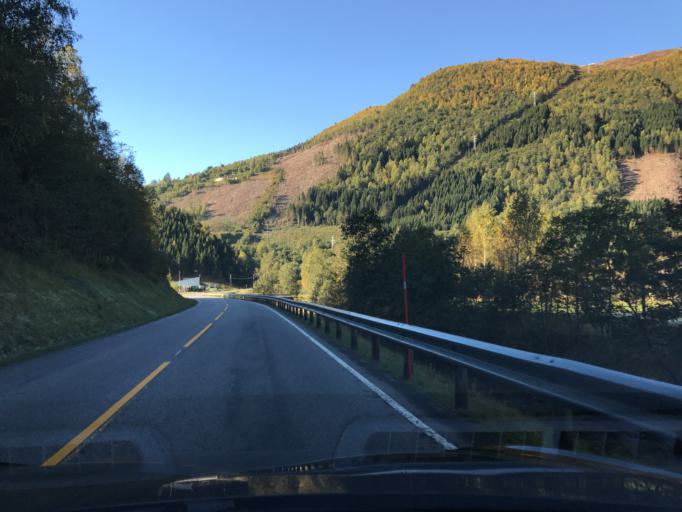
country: NO
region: More og Romsdal
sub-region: Norddal
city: Valldal
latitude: 62.3088
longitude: 7.2632
